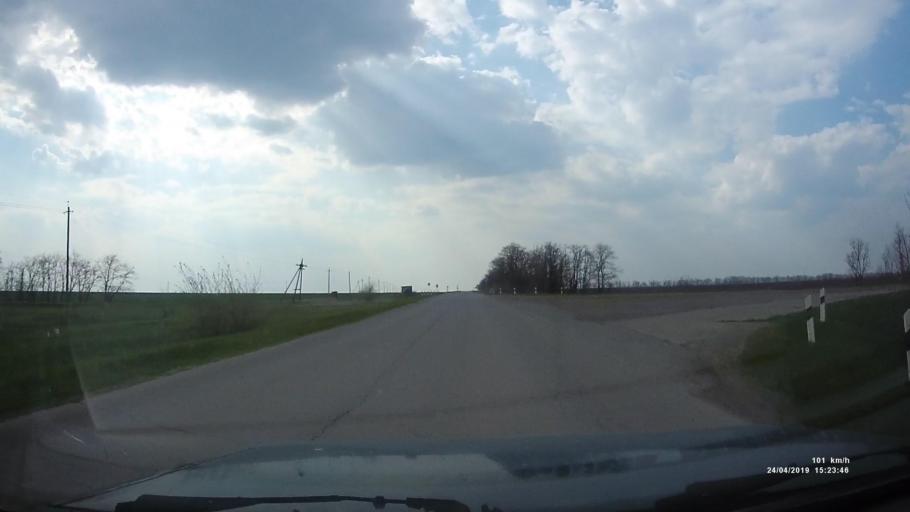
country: RU
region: Rostov
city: Remontnoye
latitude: 46.5447
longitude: 43.0832
